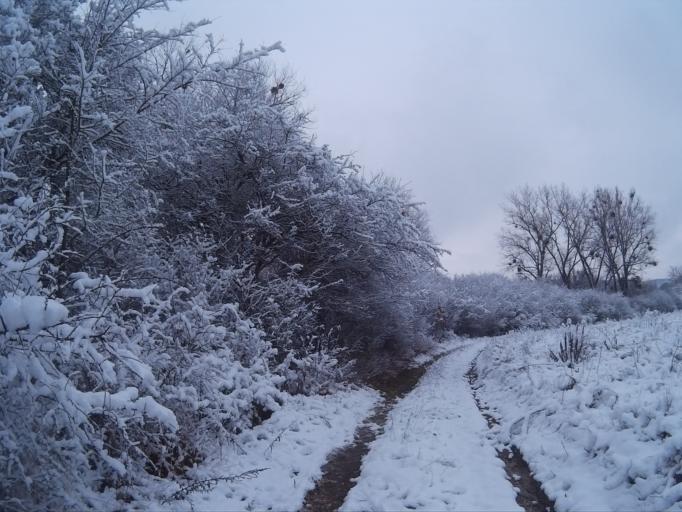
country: HU
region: Fejer
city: Szarliget
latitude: 47.5348
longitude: 18.5380
